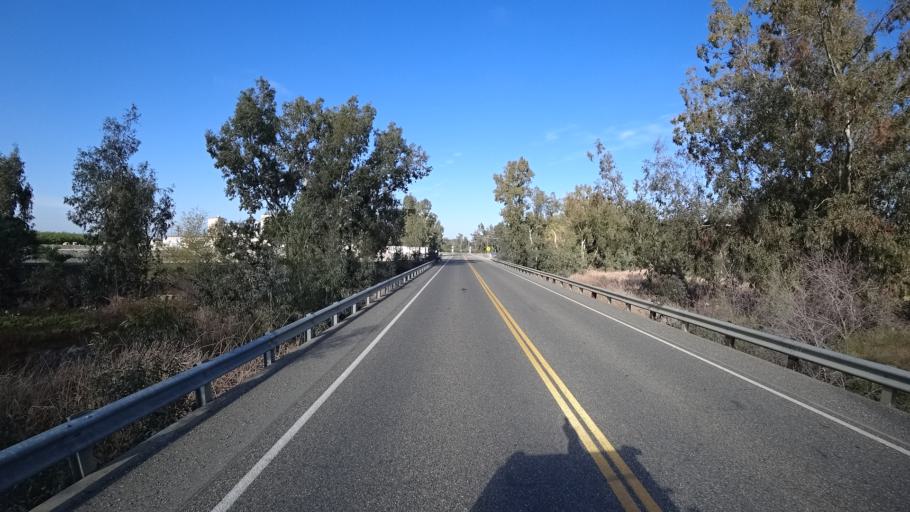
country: US
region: California
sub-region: Glenn County
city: Willows
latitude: 39.5839
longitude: -122.1911
